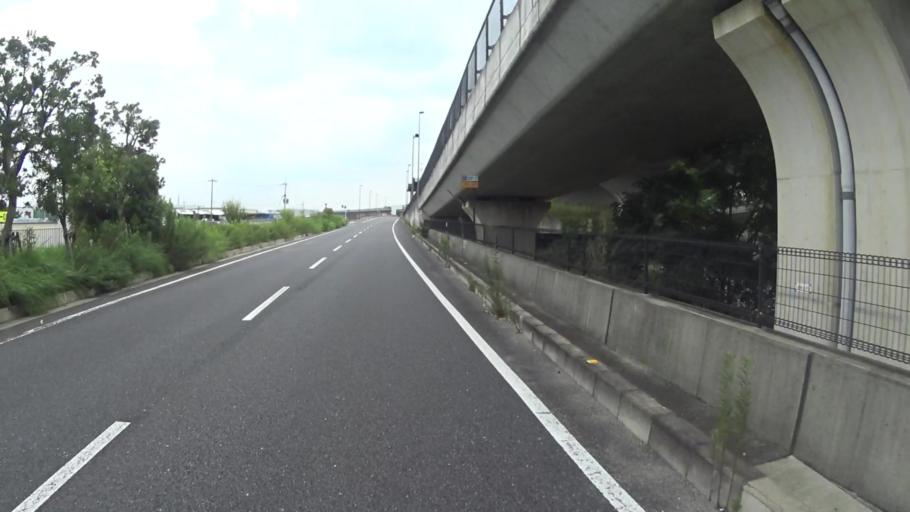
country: JP
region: Kyoto
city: Yawata
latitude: 34.8667
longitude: 135.7391
